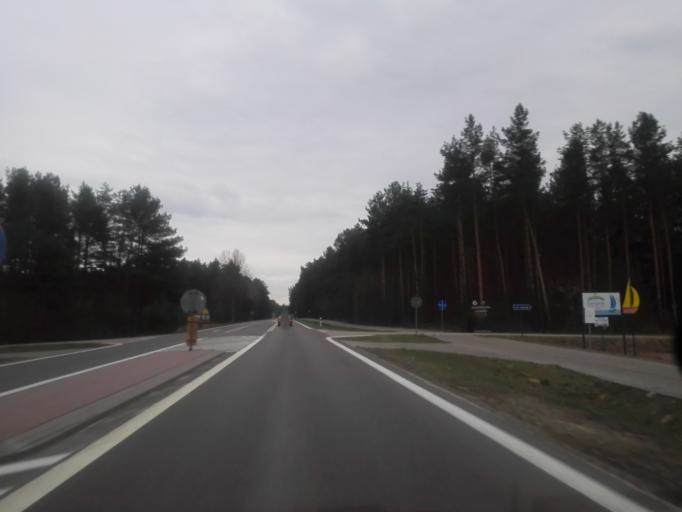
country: PL
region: Podlasie
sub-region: Powiat grajewski
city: Rajgrod
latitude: 53.7146
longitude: 22.6729
